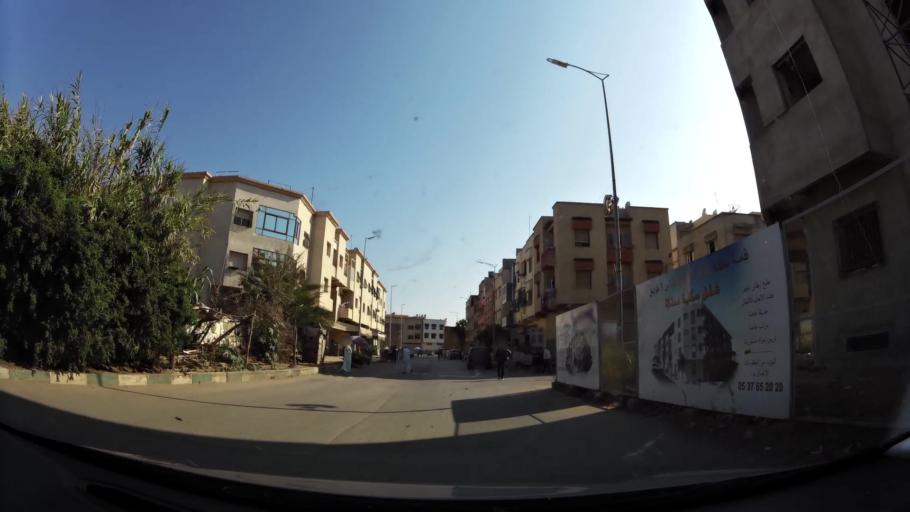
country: MA
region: Rabat-Sale-Zemmour-Zaer
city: Sale
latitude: 34.0479
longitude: -6.8125
